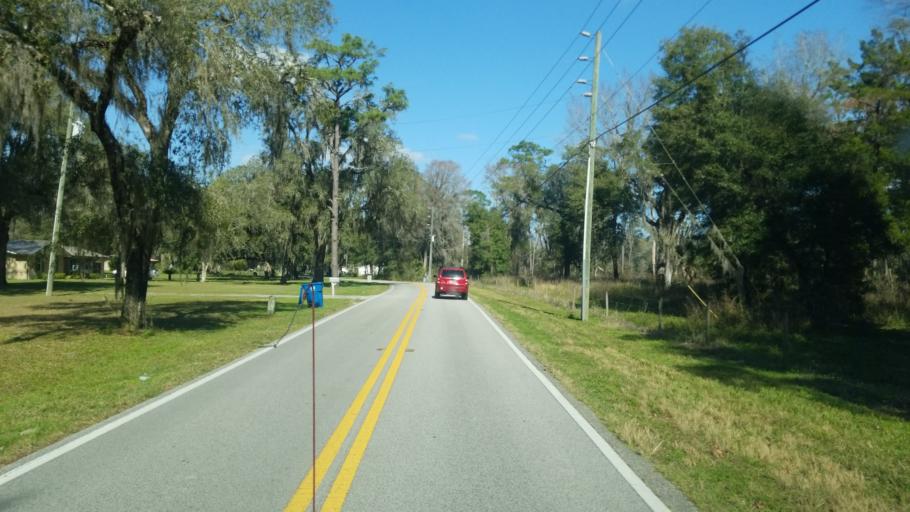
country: US
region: Florida
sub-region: Hernando County
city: North Brooksville
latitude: 28.5939
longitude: -82.3758
